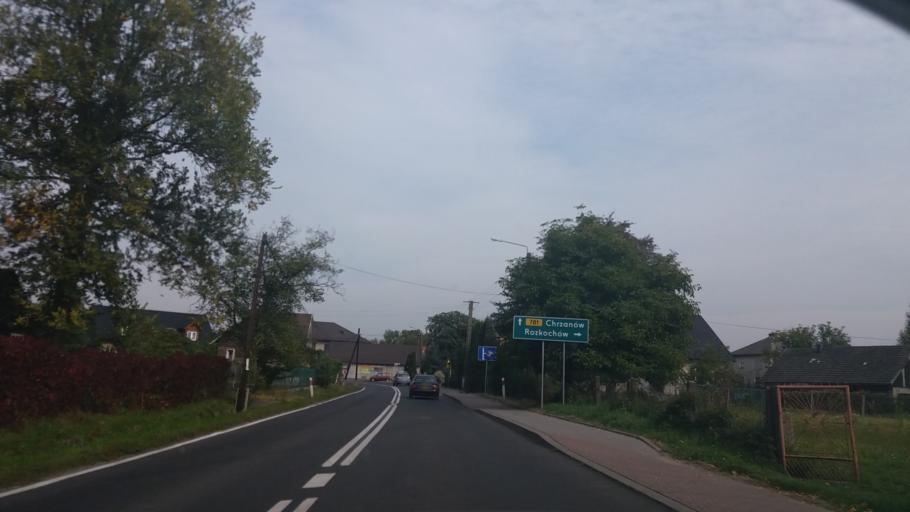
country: PL
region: Lesser Poland Voivodeship
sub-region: Powiat chrzanowski
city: Babice
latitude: 50.0525
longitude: 19.4510
